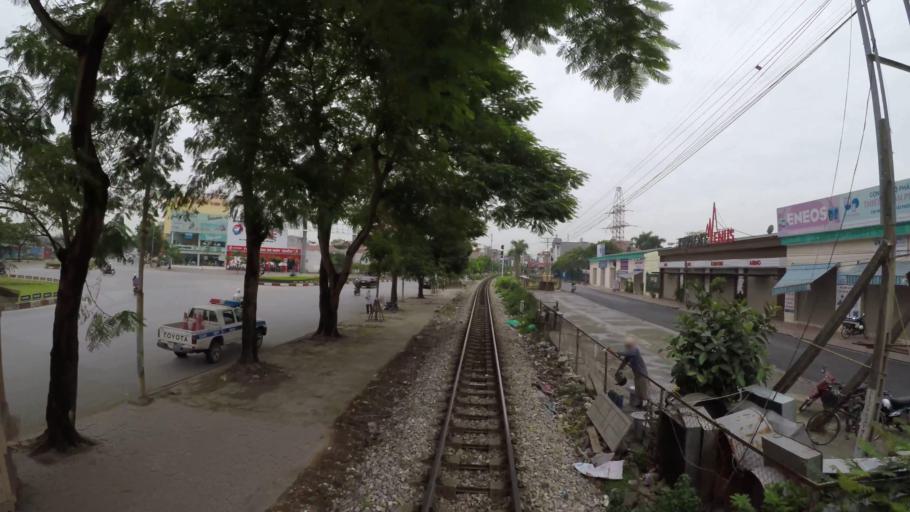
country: VN
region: Hai Phong
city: An Duong
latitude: 20.8755
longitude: 106.6372
